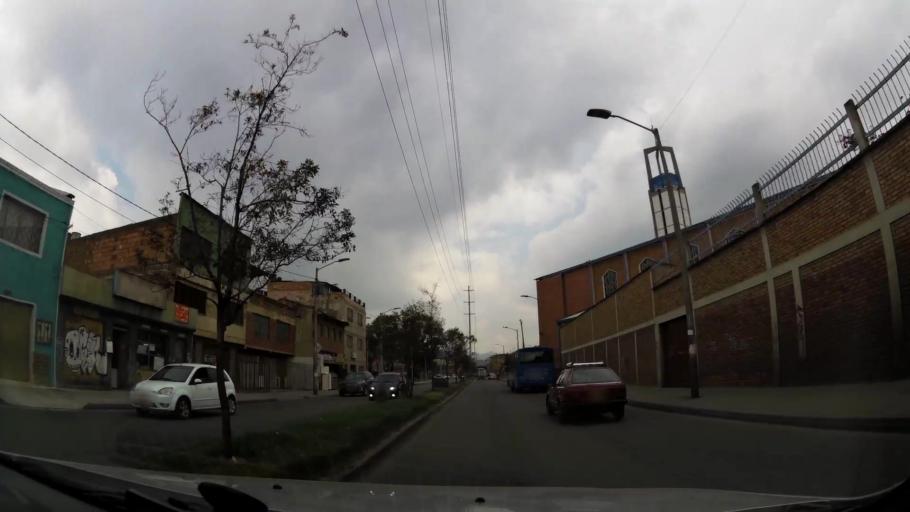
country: CO
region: Bogota D.C.
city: Bogota
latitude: 4.5844
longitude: -74.1276
